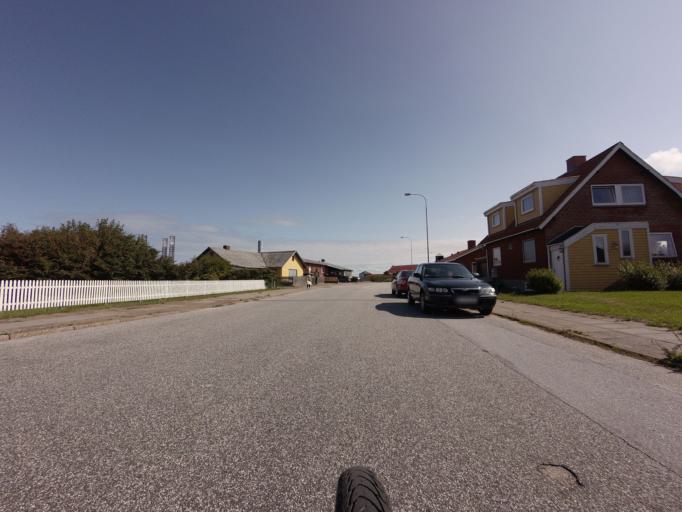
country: DK
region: North Denmark
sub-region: Hjorring Kommune
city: Hirtshals
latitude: 57.5893
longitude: 9.9684
